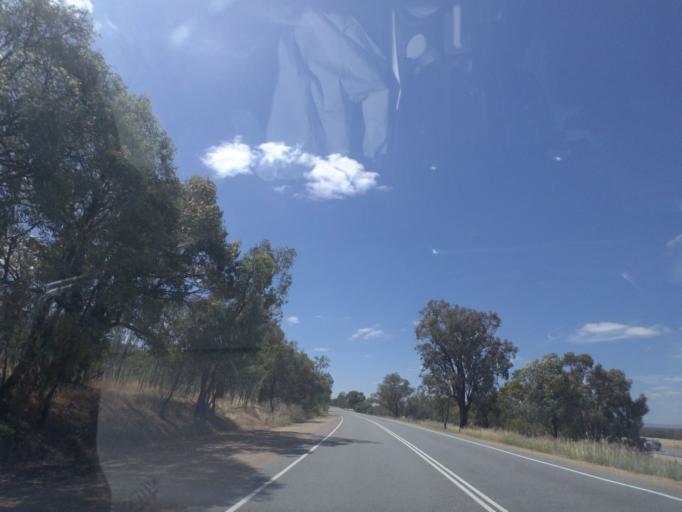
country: AU
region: Victoria
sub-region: Wangaratta
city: Wangaratta
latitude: -36.4573
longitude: 146.2364
